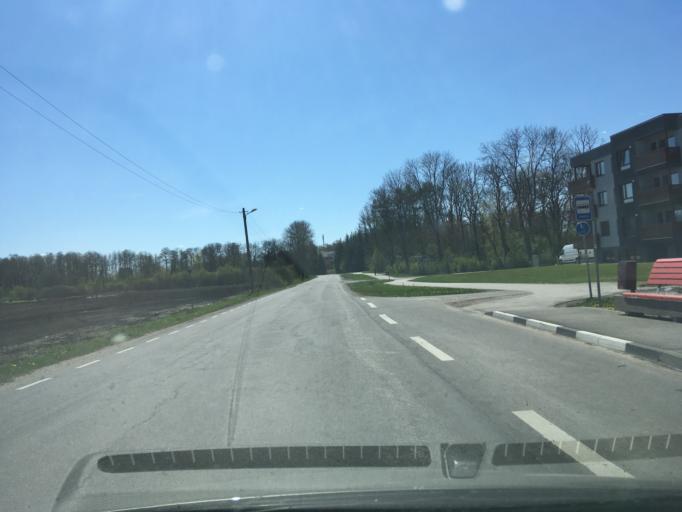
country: EE
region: Harju
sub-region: Raasiku vald
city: Arukula
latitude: 59.3627
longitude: 25.0826
